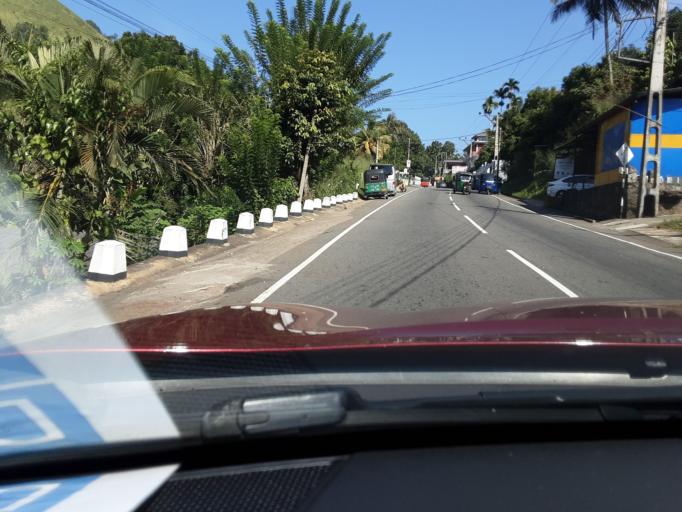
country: LK
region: Uva
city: Badulla
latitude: 7.0080
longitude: 81.0569
